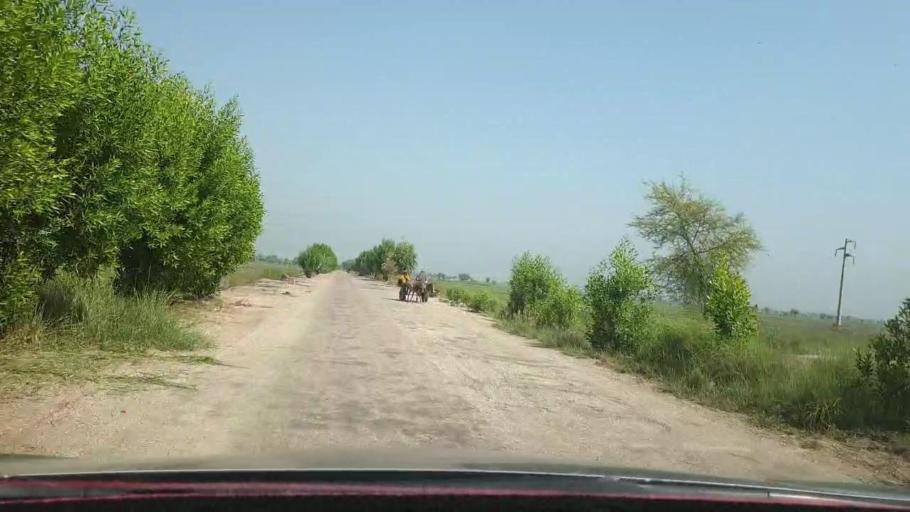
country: PK
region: Sindh
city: Warah
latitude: 27.4652
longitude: 67.8344
